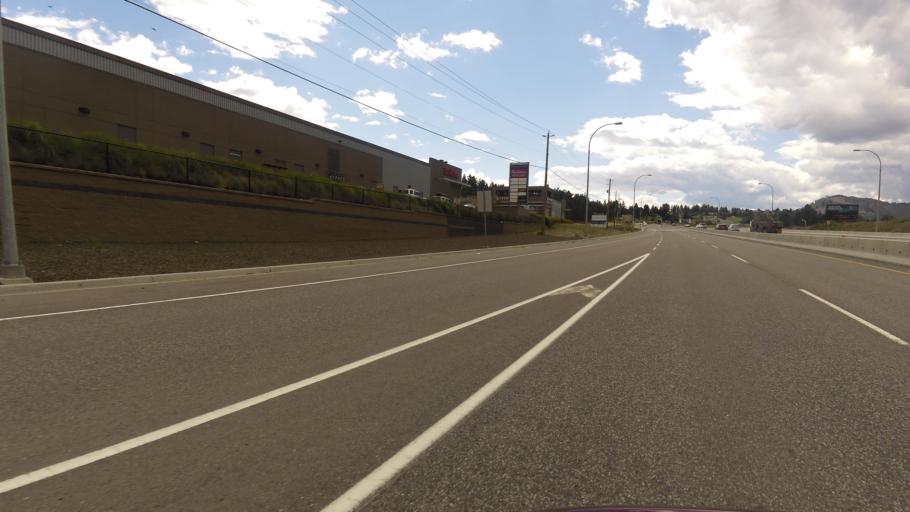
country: CA
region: British Columbia
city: West Kelowna
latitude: 49.8798
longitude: -119.5375
